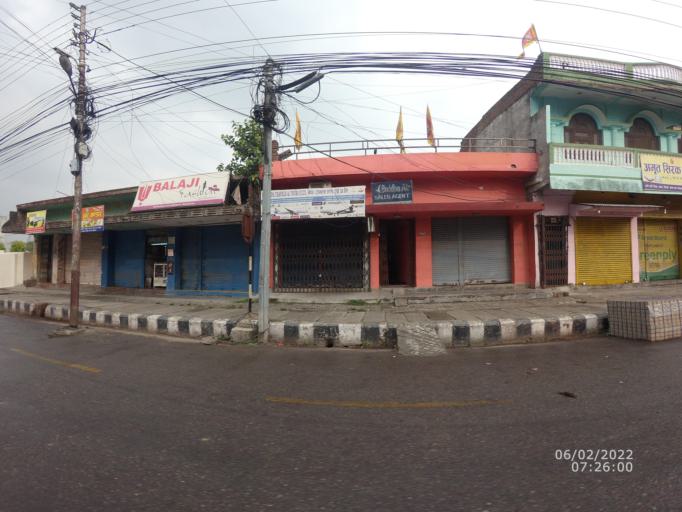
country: NP
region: Western Region
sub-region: Lumbini Zone
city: Bhairahawa
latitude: 27.5041
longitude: 83.4500
